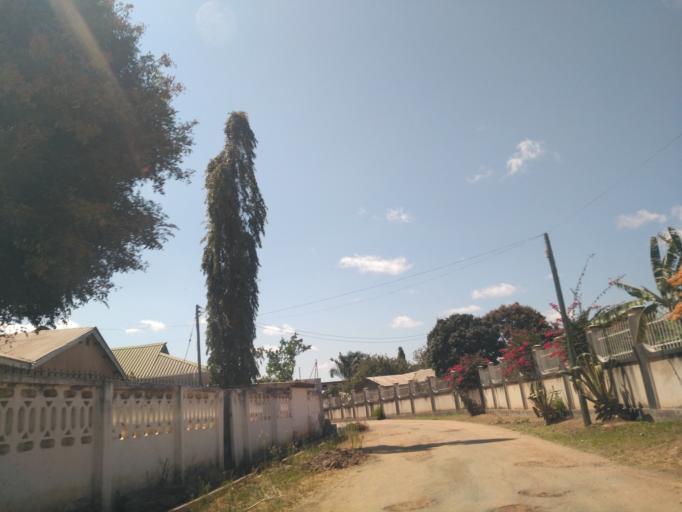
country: TZ
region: Dodoma
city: Dodoma
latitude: -6.1614
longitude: 35.7577
